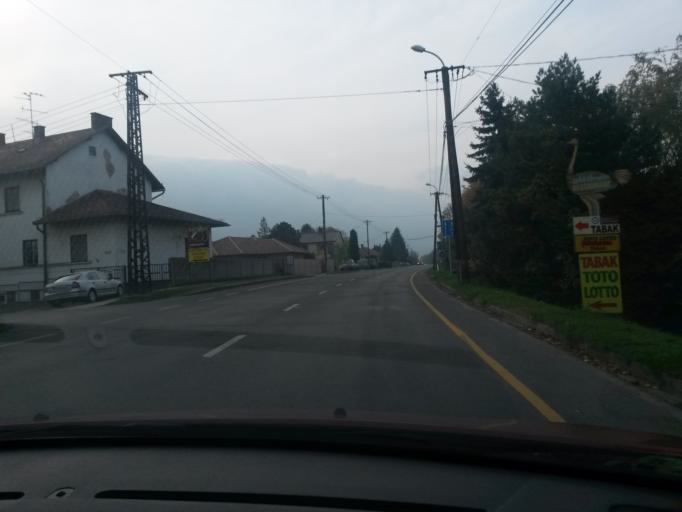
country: AT
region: Burgenland
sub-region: Politischer Bezirk Neusiedl am See
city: Nickelsdorf
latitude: 47.9155
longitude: 17.1517
